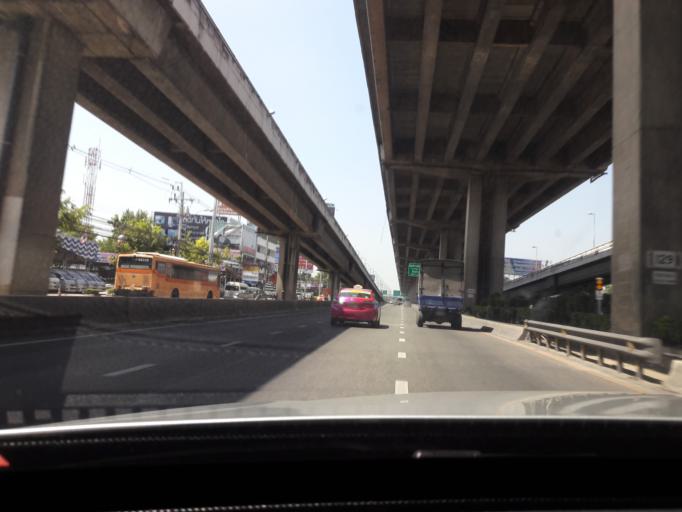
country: TH
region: Bangkok
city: Taling Chan
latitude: 13.7817
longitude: 100.4212
